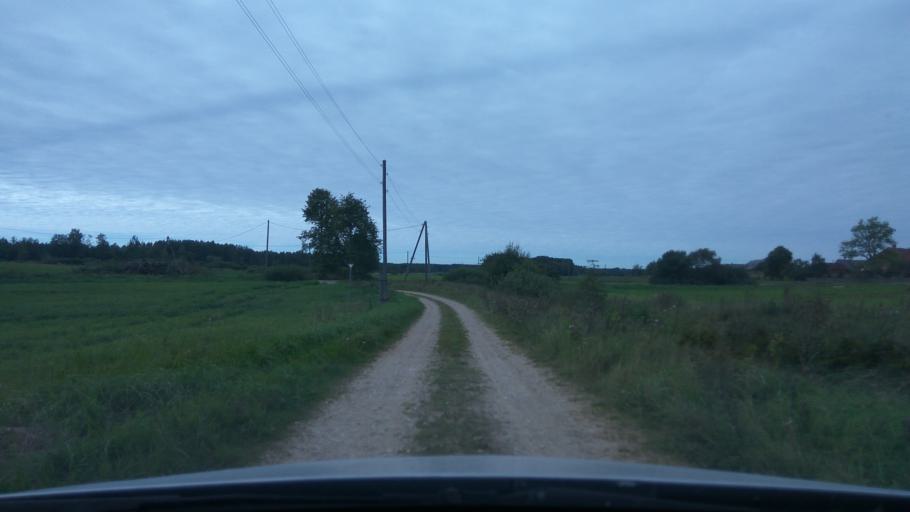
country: LV
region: Kuldigas Rajons
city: Kuldiga
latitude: 57.2420
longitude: 21.9510
